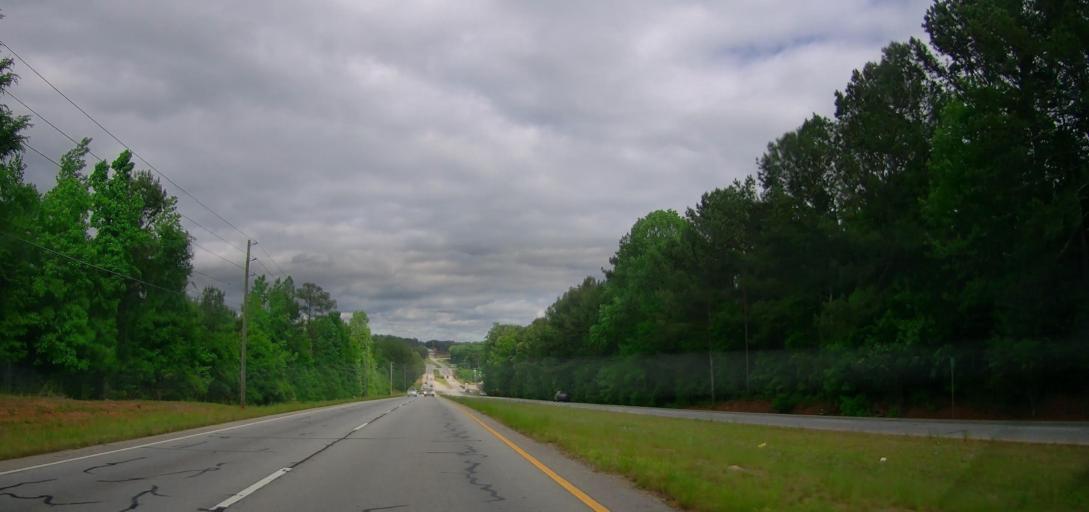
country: US
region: Georgia
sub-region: Walton County
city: Monroe
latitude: 33.8062
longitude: -83.7658
